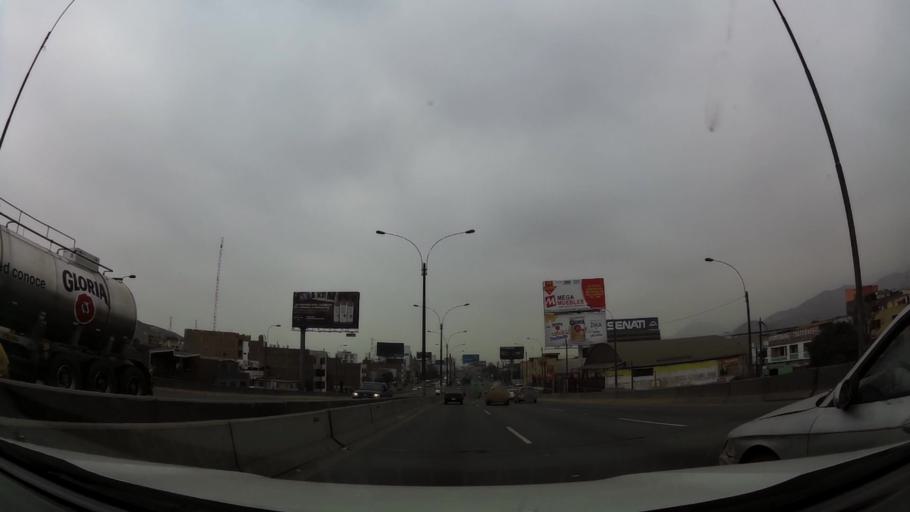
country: PE
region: Lima
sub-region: Lima
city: Independencia
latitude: -12.0029
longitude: -77.0620
